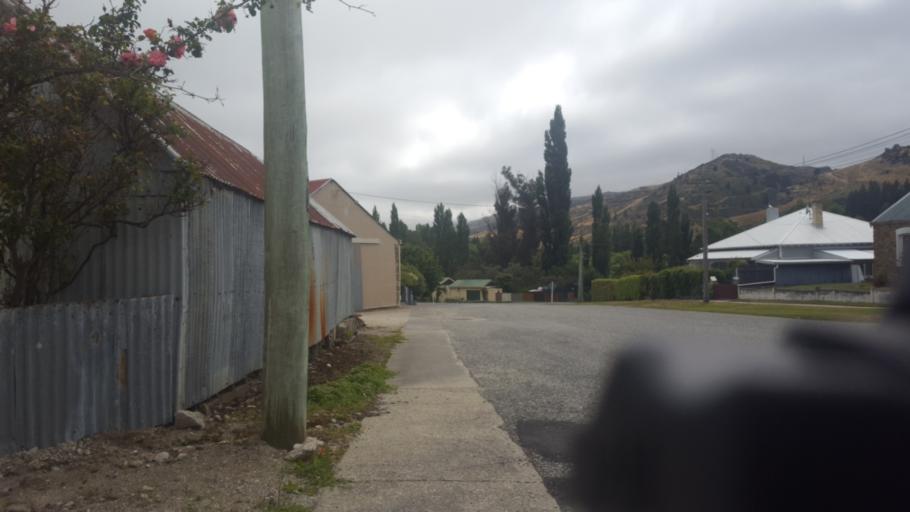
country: NZ
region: Otago
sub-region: Queenstown-Lakes District
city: Kingston
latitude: -45.5413
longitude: 169.3157
